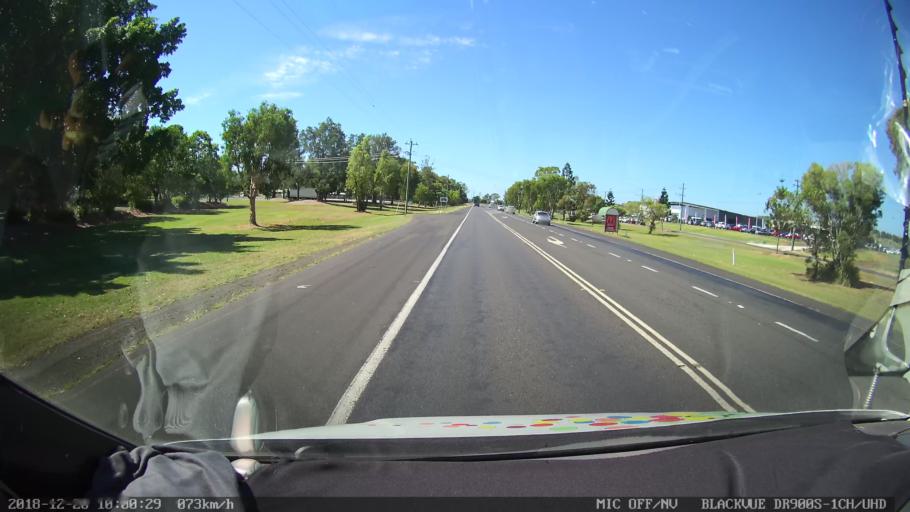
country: AU
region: New South Wales
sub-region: Lismore Municipality
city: Lismore
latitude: -28.8331
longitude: 153.2648
